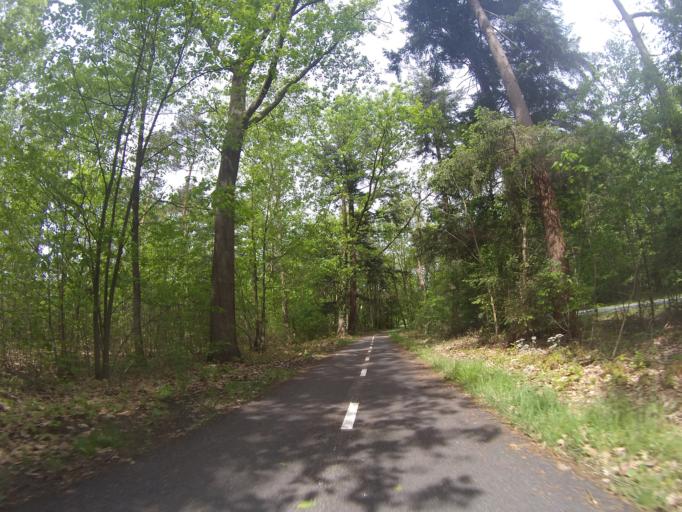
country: NL
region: Drenthe
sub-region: Gemeente Borger-Odoorn
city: Borger
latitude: 52.8994
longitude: 6.7043
